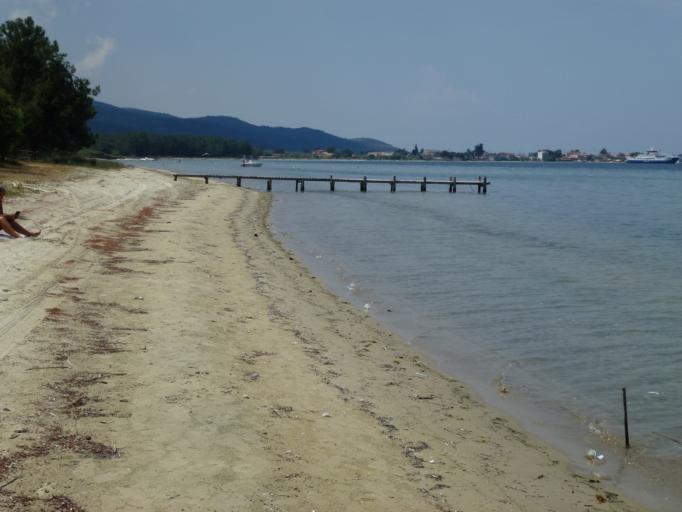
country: GR
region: East Macedonia and Thrace
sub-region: Nomos Kavalas
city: Prinos
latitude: 40.7693
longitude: 24.5920
